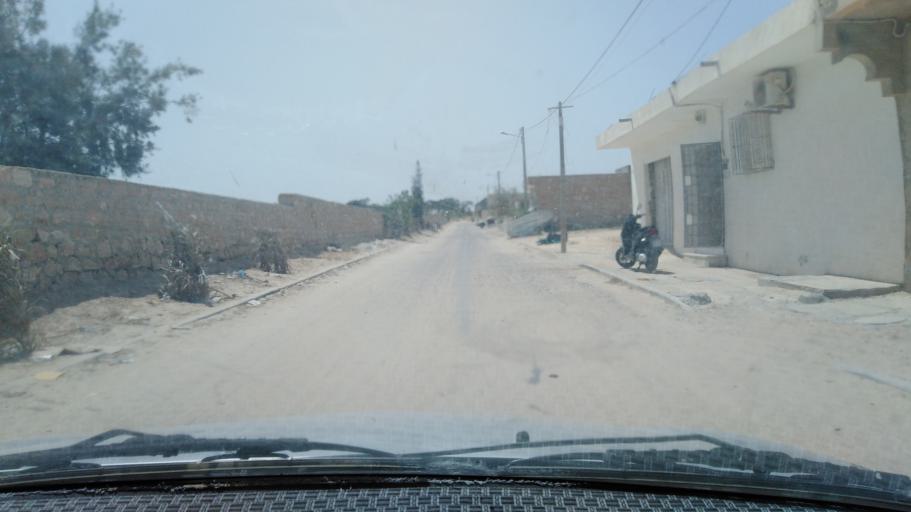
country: TN
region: Qabis
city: Gabes
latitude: 33.9556
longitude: 9.9984
